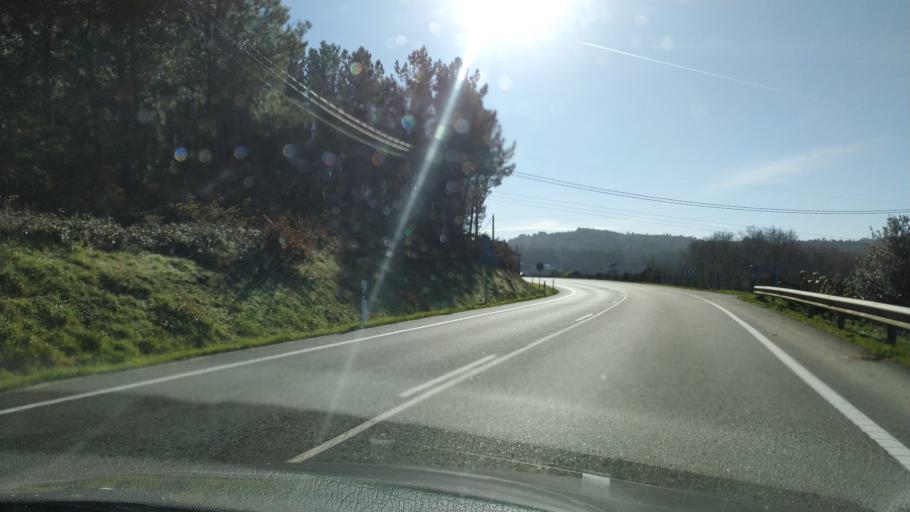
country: ES
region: Galicia
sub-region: Provincia da Coruna
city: Ribeira
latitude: 42.7533
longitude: -8.3536
